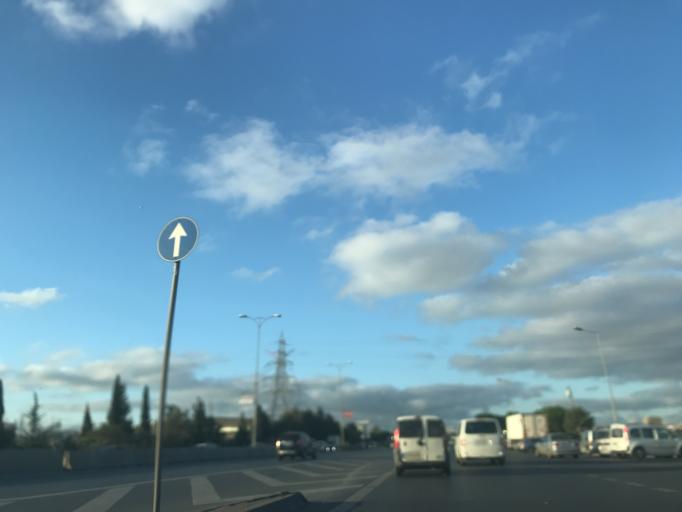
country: TR
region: Istanbul
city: Esenler
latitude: 41.0495
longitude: 28.8854
